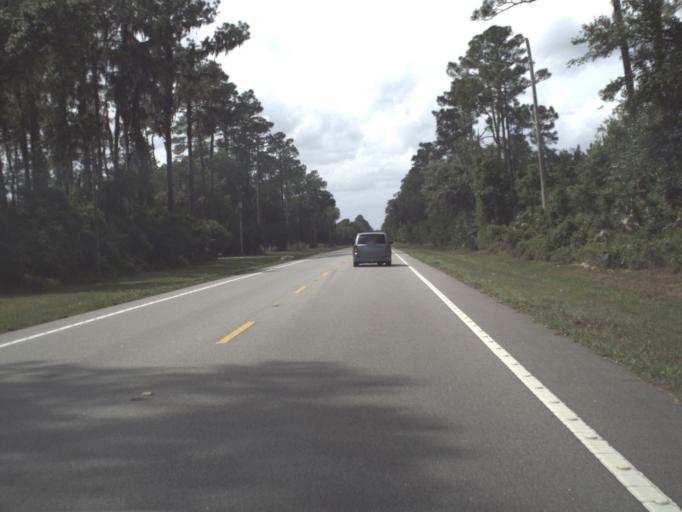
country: US
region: Florida
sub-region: Putnam County
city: Crescent City
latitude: 29.5026
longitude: -81.4879
